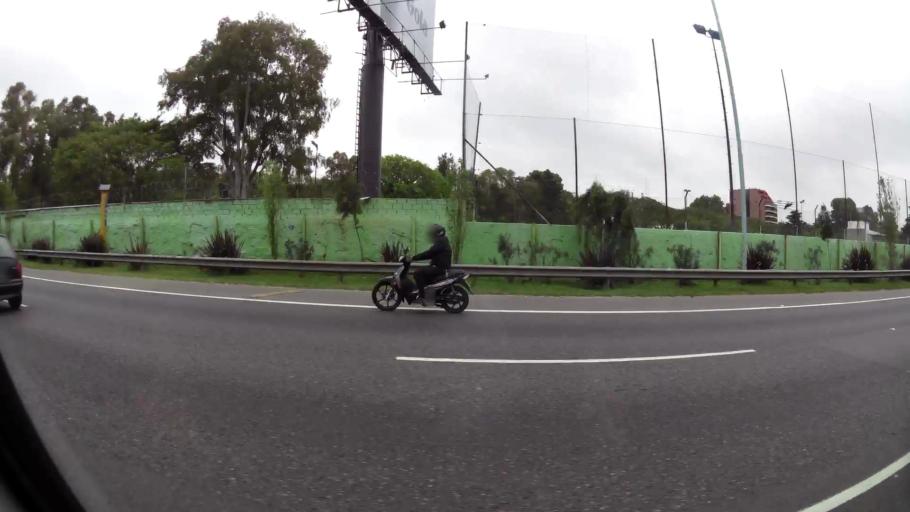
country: AR
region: Buenos Aires F.D.
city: Colegiales
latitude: -34.5468
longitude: -58.4417
